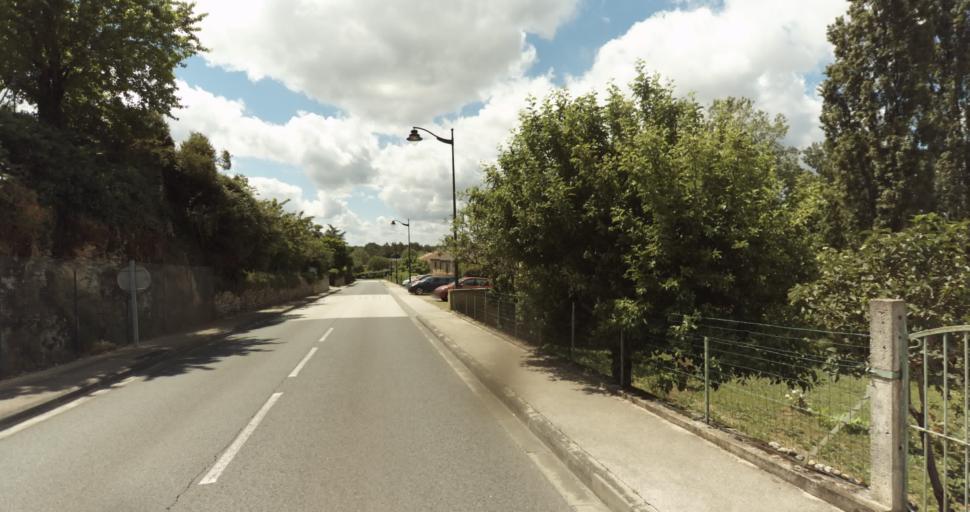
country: FR
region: Aquitaine
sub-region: Departement de la Dordogne
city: Beaumont-du-Perigord
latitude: 44.7659
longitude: 0.7671
